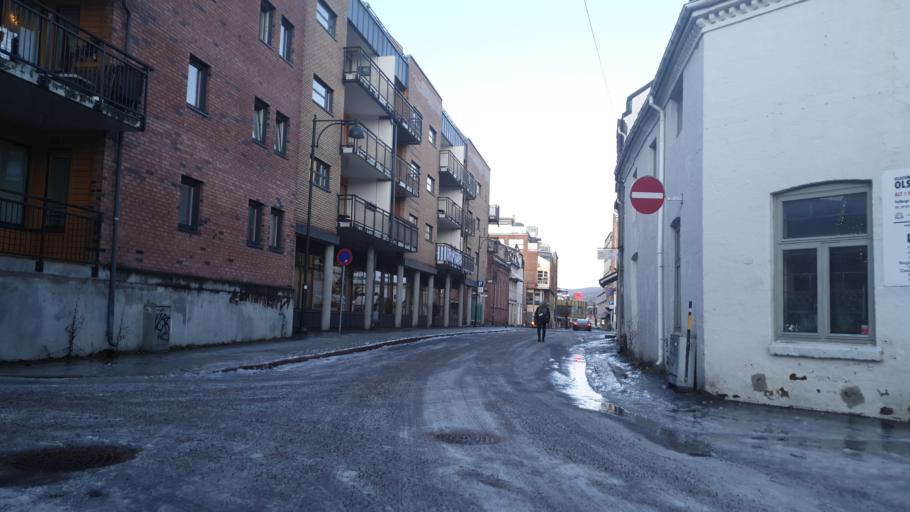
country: NO
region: Buskerud
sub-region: Drammen
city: Drammen
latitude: 59.7382
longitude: 10.2047
